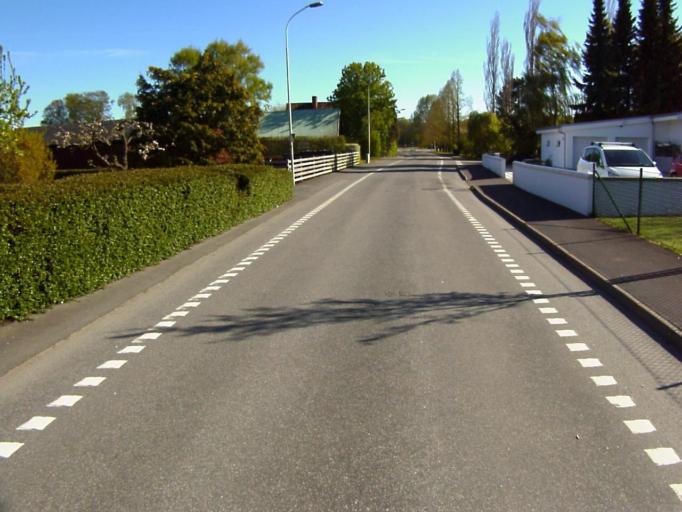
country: SE
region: Skane
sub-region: Kristianstads Kommun
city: Kristianstad
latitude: 56.0307
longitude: 14.1986
